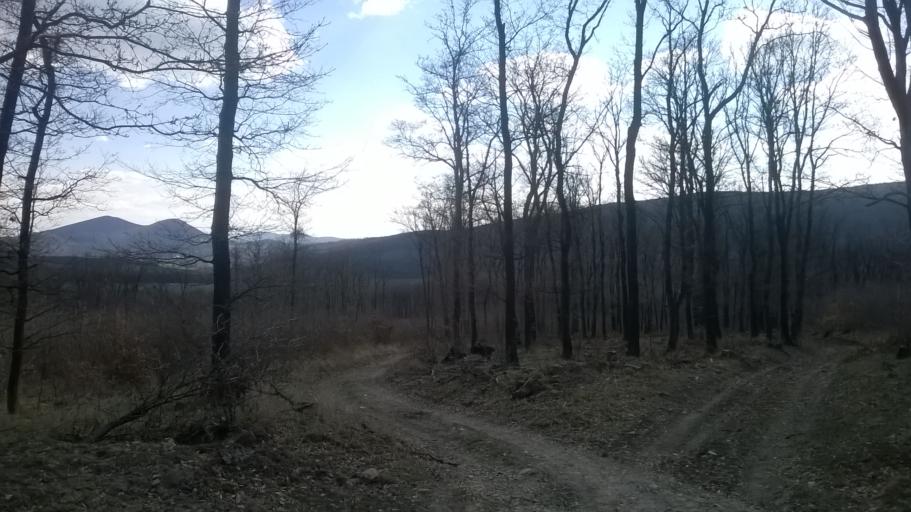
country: HU
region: Pest
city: Pilisszentkereszt
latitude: 47.6861
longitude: 18.9355
